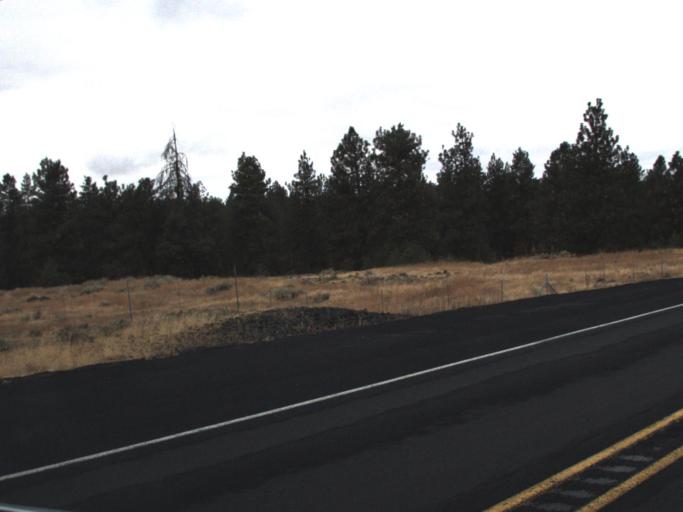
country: US
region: Washington
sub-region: Lincoln County
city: Davenport
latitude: 47.7324
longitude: -118.4672
